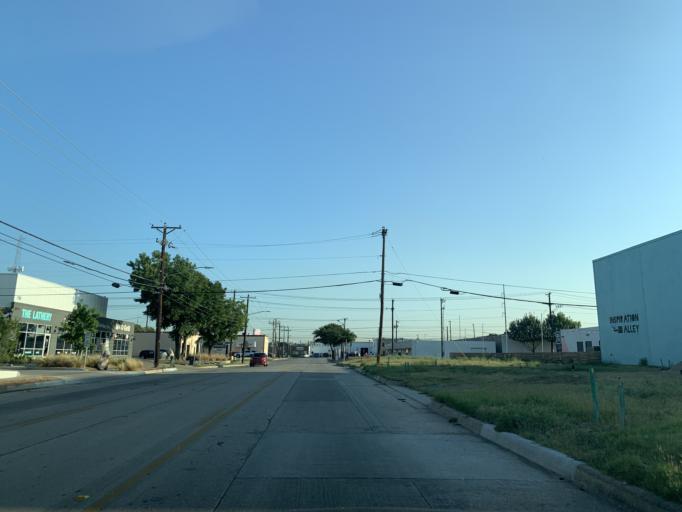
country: US
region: Texas
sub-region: Tarrant County
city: River Oaks
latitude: 32.7572
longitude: -97.3546
